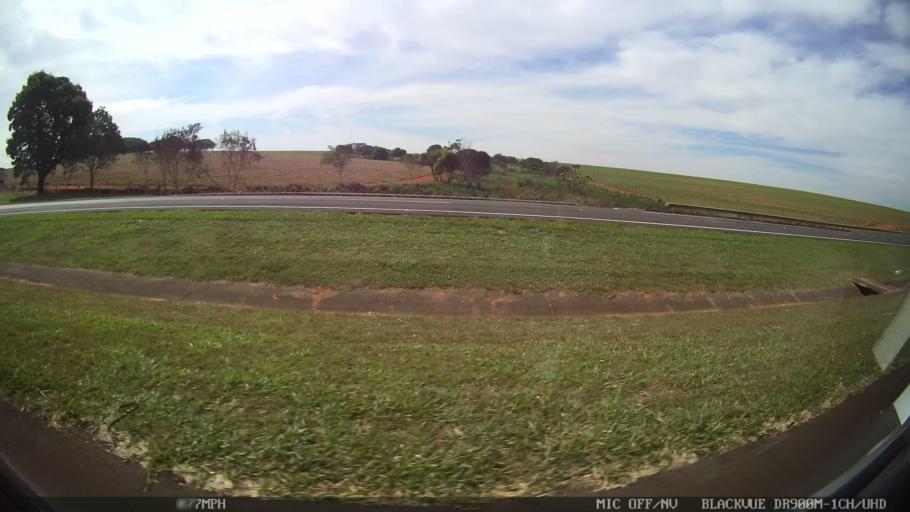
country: BR
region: Sao Paulo
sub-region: Matao
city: Matao
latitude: -21.6073
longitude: -48.4266
